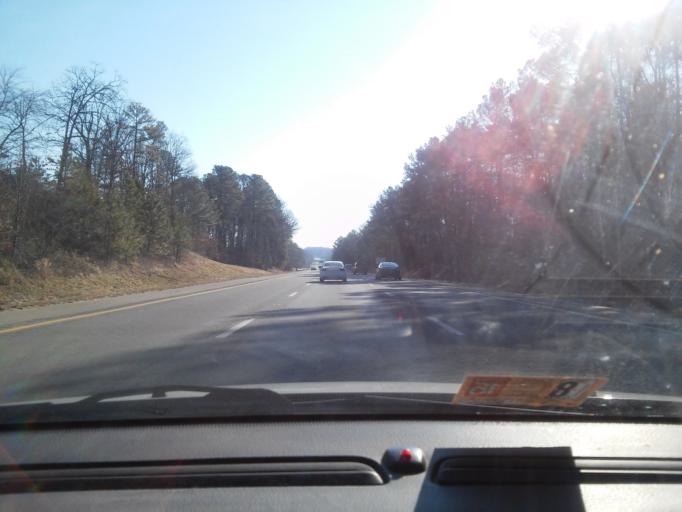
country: US
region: Virginia
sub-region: Henrico County
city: Short Pump
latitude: 37.6414
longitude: -77.5861
